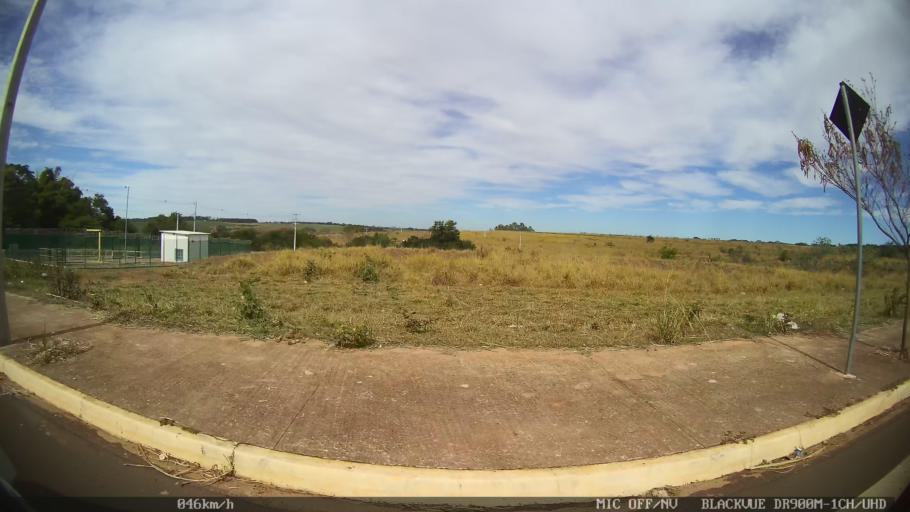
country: BR
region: Sao Paulo
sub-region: Catanduva
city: Catanduva
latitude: -21.1697
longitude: -48.9623
